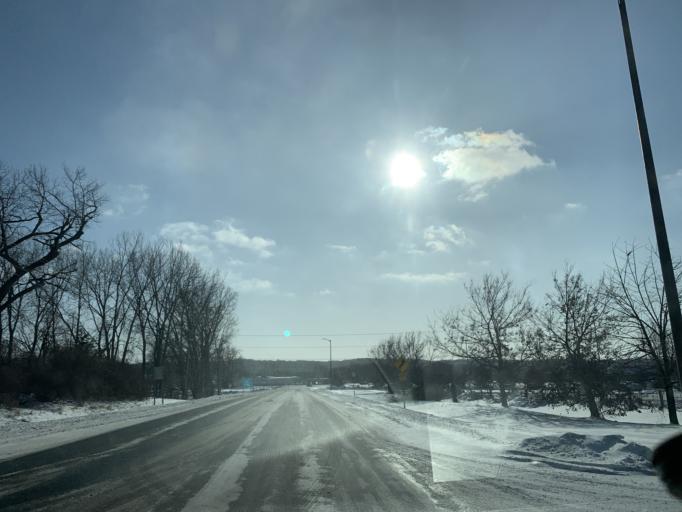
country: US
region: Minnesota
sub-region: Scott County
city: Prior Lake
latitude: 44.7804
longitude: -93.4069
